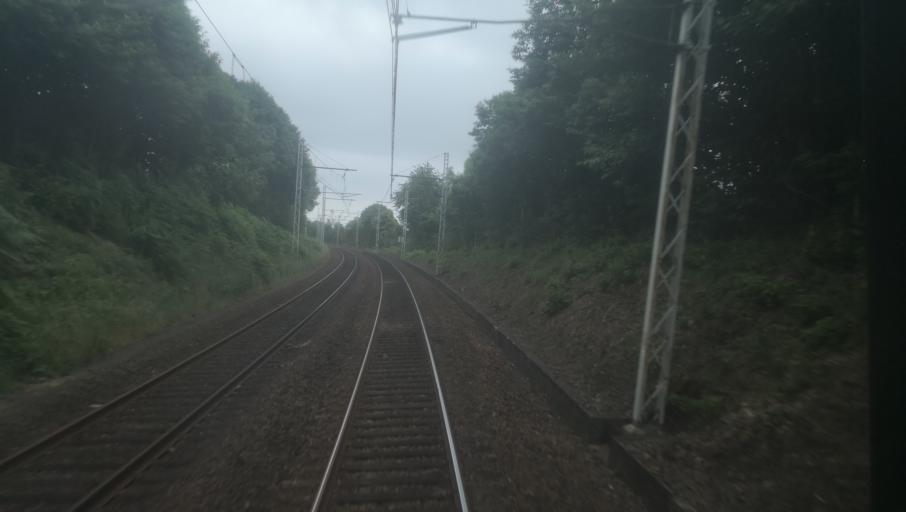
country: FR
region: Centre
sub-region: Departement de l'Indre
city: Chantome
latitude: 46.3893
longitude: 1.5489
